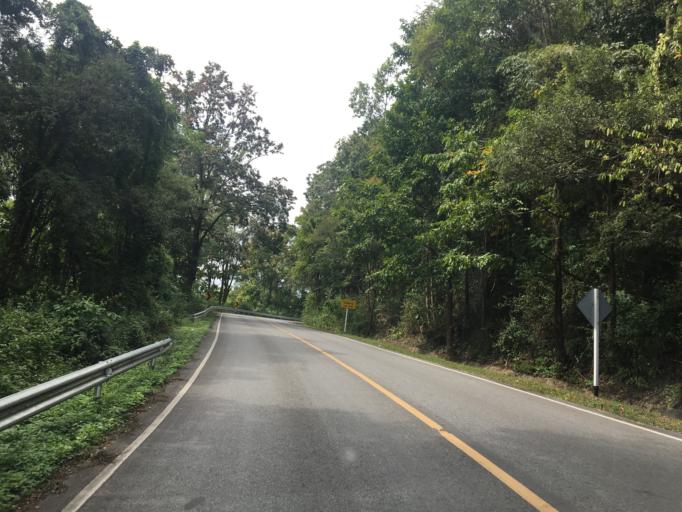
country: TH
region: Nan
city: Ban Luang
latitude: 18.8756
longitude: 100.5441
